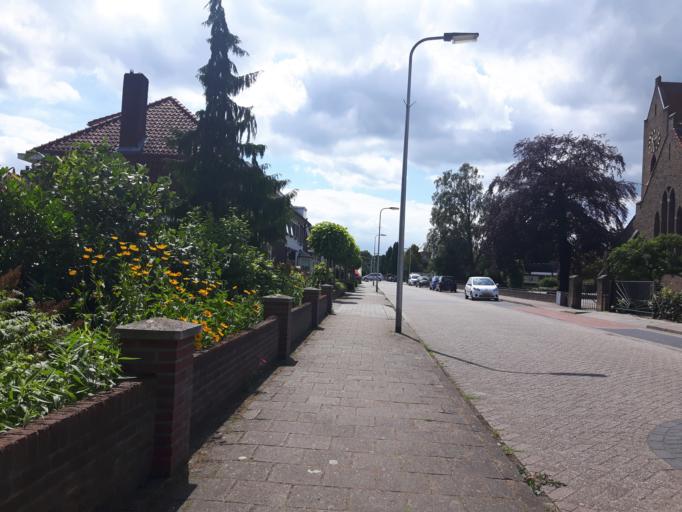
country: NL
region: Overijssel
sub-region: Gemeente Haaksbergen
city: Haaksbergen
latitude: 52.1645
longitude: 6.7571
